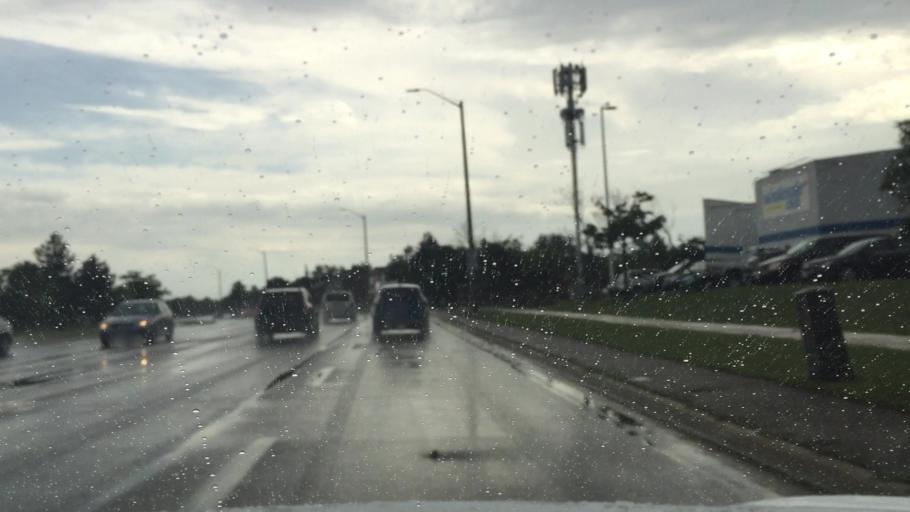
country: CA
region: Ontario
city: Mississauga
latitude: 43.5828
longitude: -79.6388
